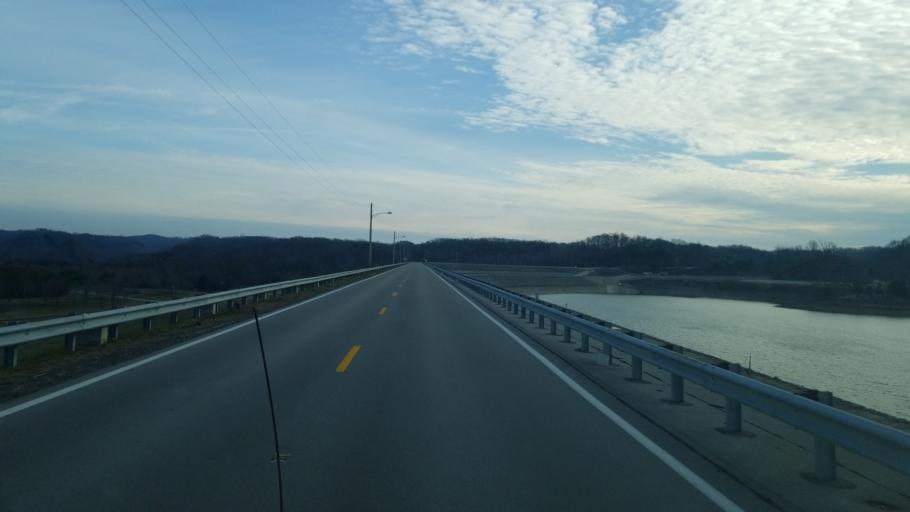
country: US
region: Kentucky
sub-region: Russell County
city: Jamestown
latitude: 36.8706
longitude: -85.1409
